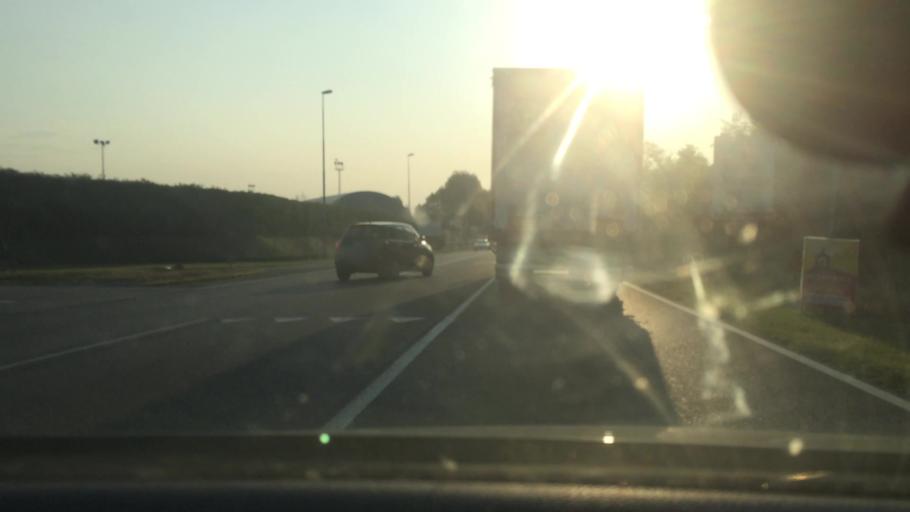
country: IT
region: Lombardy
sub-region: Citta metropolitana di Milano
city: Parabiago
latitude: 45.5474
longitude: 8.9354
